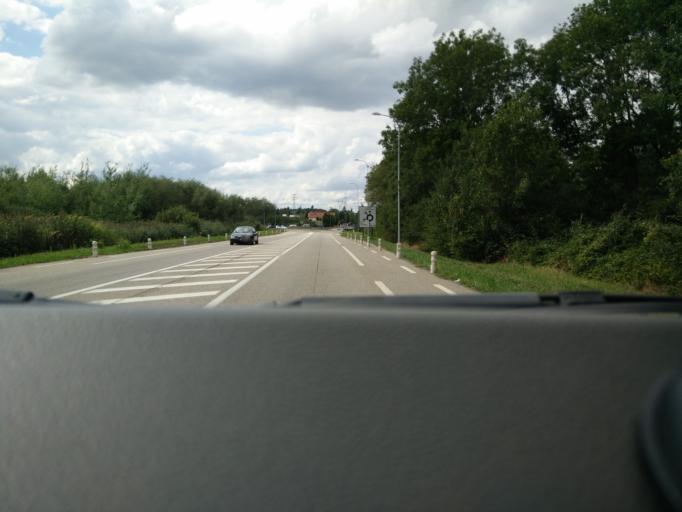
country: FR
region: Lorraine
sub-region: Departement de Meurthe-et-Moselle
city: Art-sur-Meurthe
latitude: 48.6430
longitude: 6.2559
